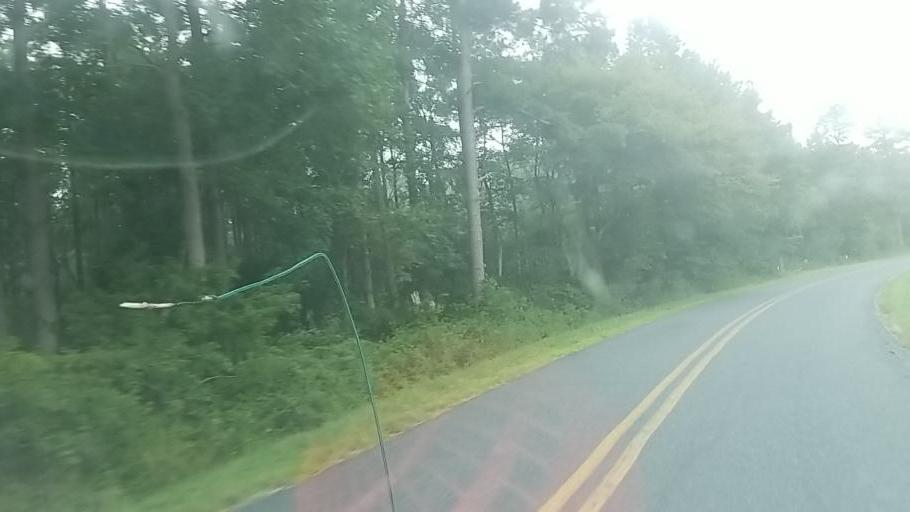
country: US
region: Maryland
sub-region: Wicomico County
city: Pittsville
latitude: 38.4148
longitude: -75.4980
